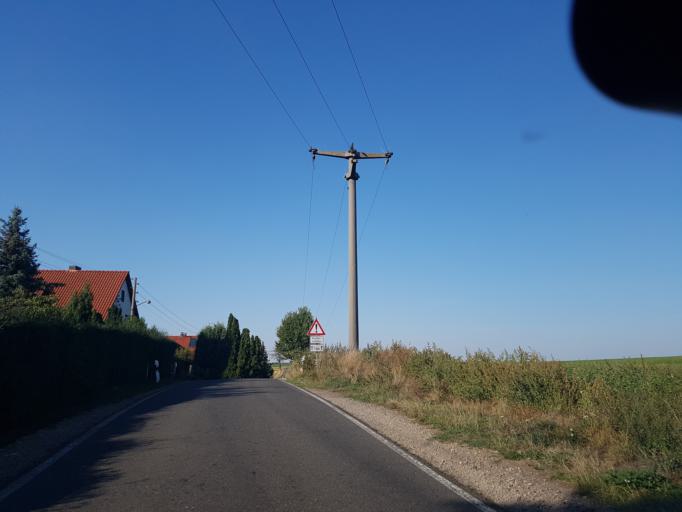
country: DE
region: Saxony
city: Dobeln
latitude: 51.1700
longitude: 13.1142
